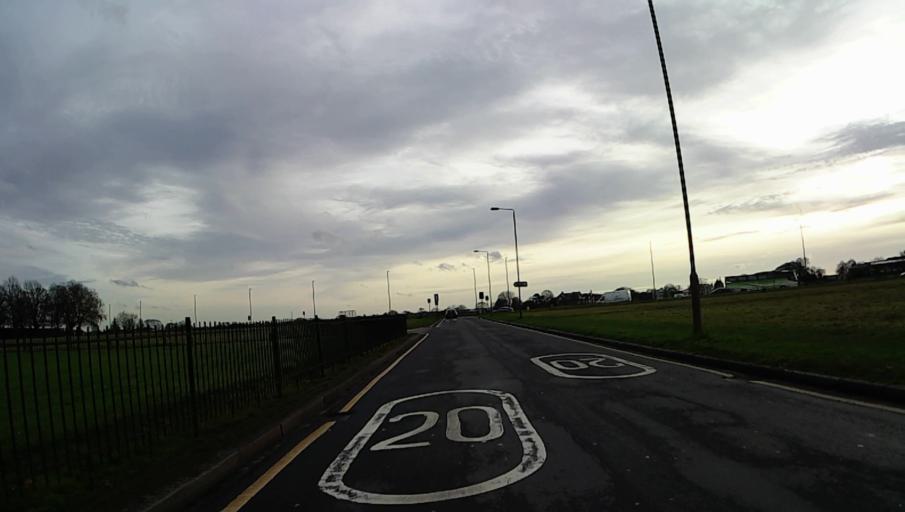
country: GB
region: England
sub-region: Greater London
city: Blackheath
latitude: 51.4730
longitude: -0.0029
